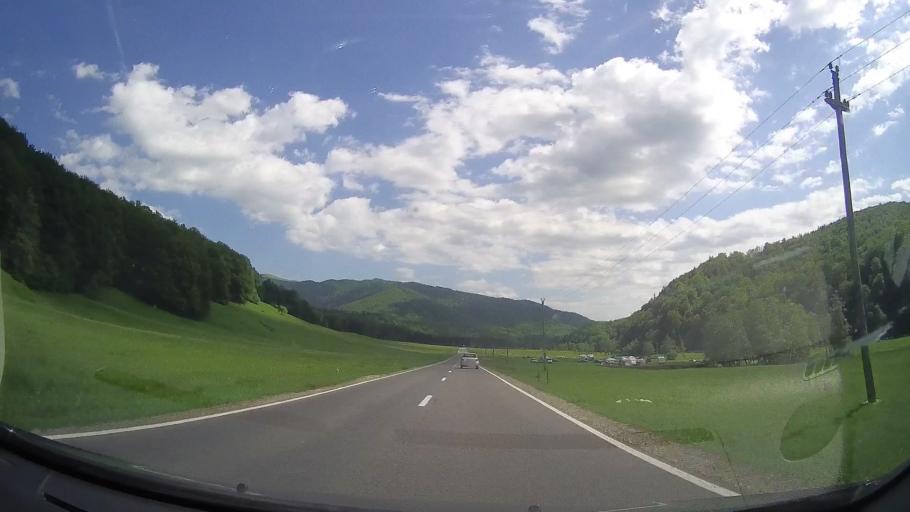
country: RO
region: Prahova
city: Maneciu
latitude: 45.4272
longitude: 25.9403
